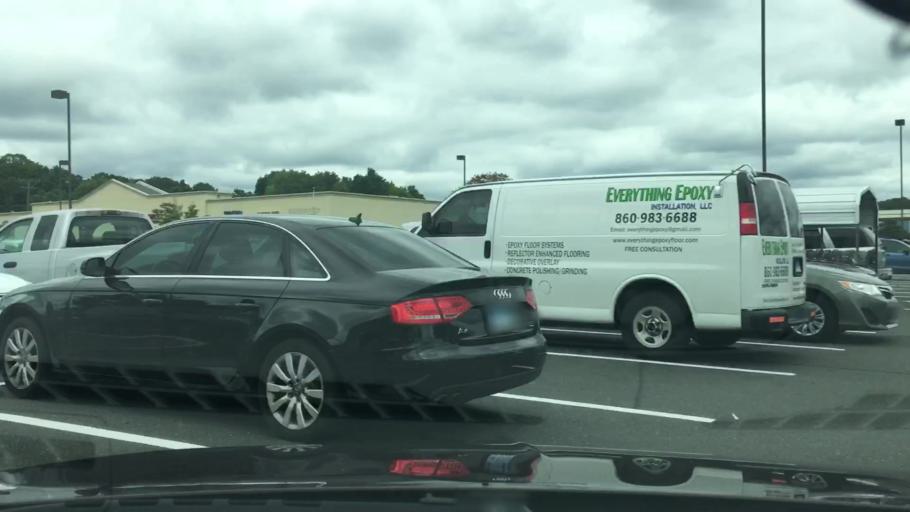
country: US
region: Connecticut
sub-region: Hartford County
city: Manchester
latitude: 41.7947
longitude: -72.5479
